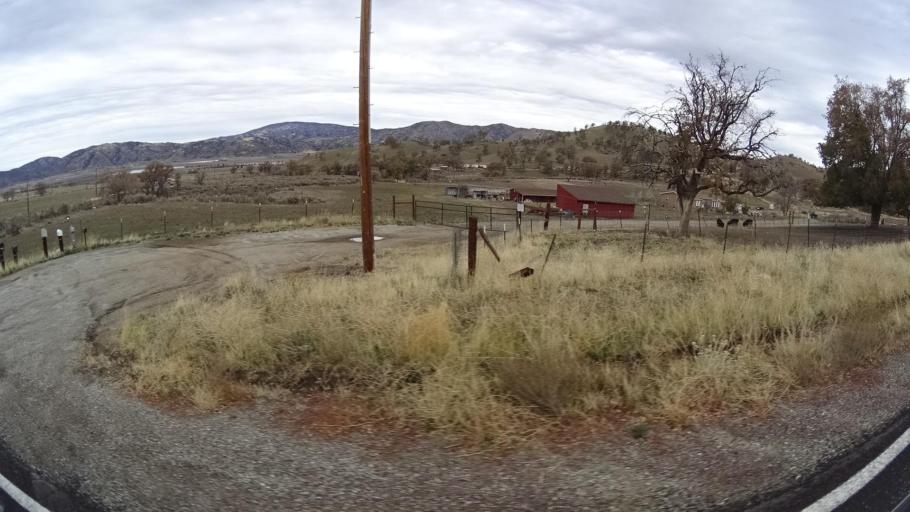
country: US
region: California
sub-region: Kern County
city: Stallion Springs
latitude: 35.0920
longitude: -118.5668
